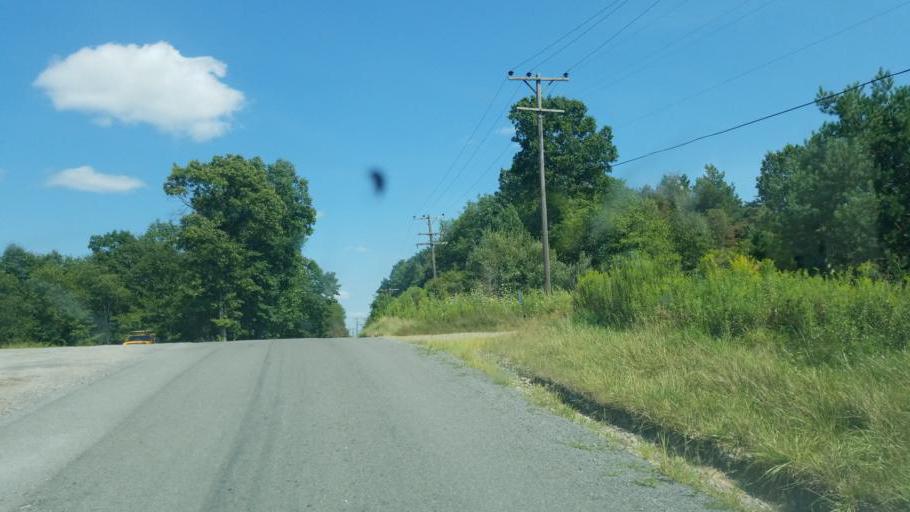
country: US
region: Pennsylvania
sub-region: Clarion County
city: Knox
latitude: 41.0975
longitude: -79.4918
